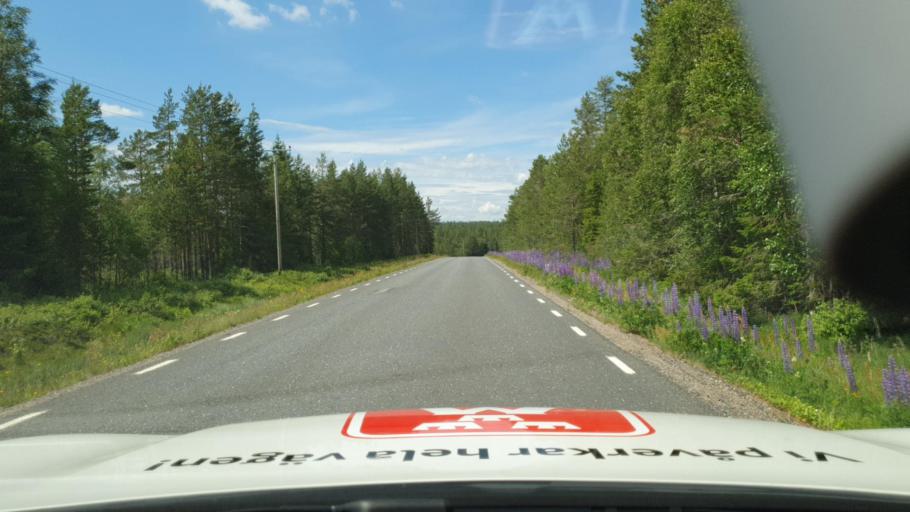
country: SE
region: Vaermland
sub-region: Torsby Kommun
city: Torsby
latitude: 60.5093
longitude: 12.8420
